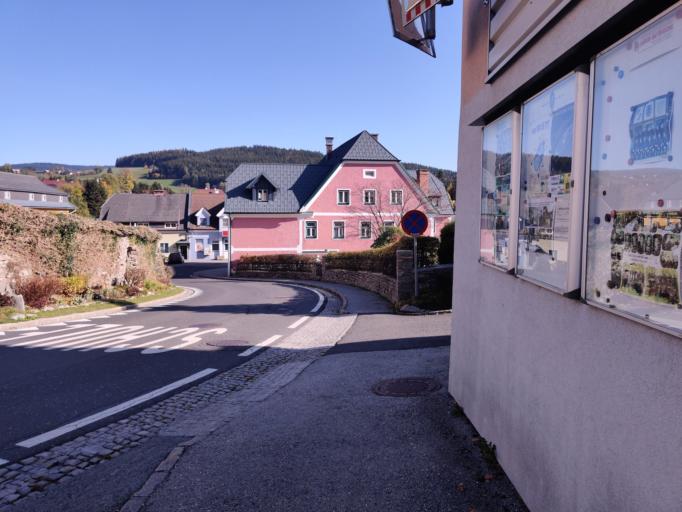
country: AT
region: Styria
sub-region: Politischer Bezirk Hartberg-Fuerstenfeld
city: Sankt Jakob im Walde
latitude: 47.4661
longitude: 15.7876
